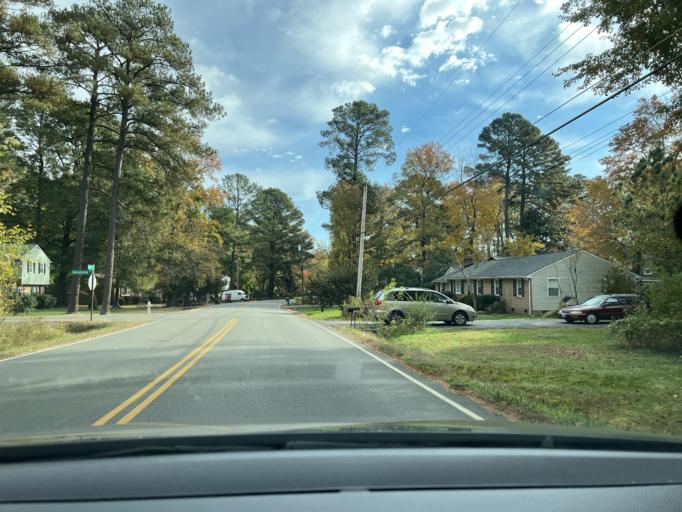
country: US
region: Virginia
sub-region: Henrico County
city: Tuckahoe
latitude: 37.6125
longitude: -77.5428
